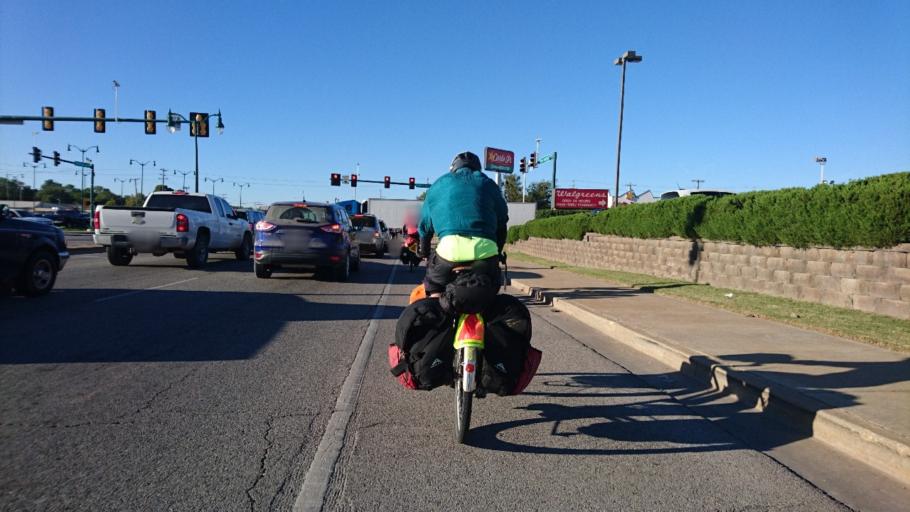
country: US
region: Oklahoma
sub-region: Rogers County
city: Claremore
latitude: 36.3122
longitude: -95.6164
